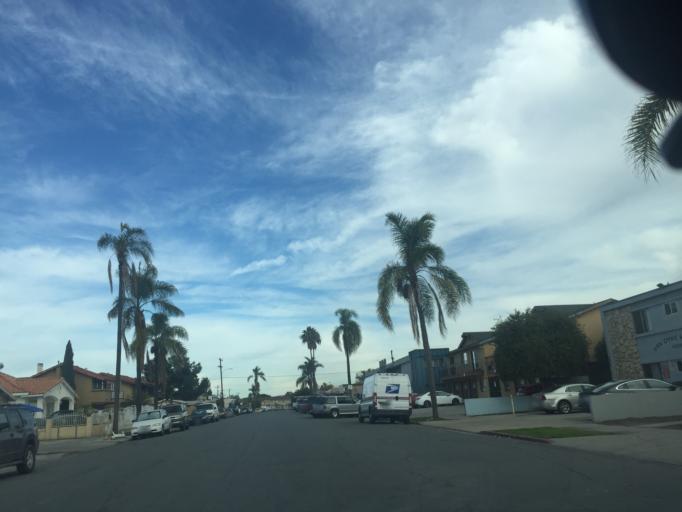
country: US
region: California
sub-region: San Diego County
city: San Diego
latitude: 32.7504
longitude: -117.1032
